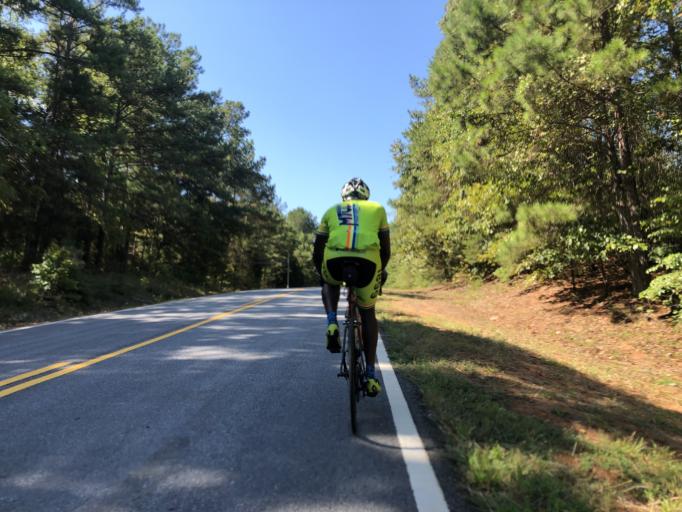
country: US
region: Georgia
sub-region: Coweta County
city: Newnan
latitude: 33.3963
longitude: -84.9616
